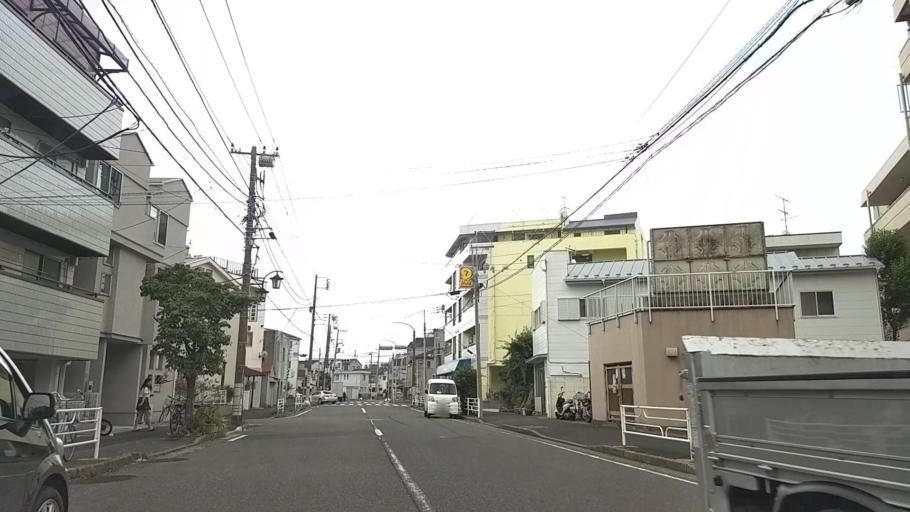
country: JP
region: Kanagawa
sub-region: Kawasaki-shi
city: Kawasaki
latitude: 35.5039
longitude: 139.6895
